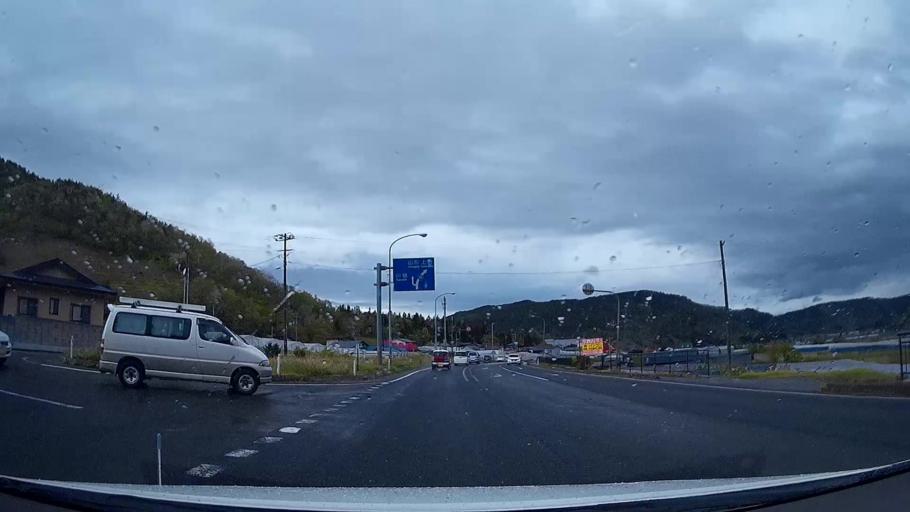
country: JP
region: Yamagata
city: Takahata
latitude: 38.0737
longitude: 140.1835
